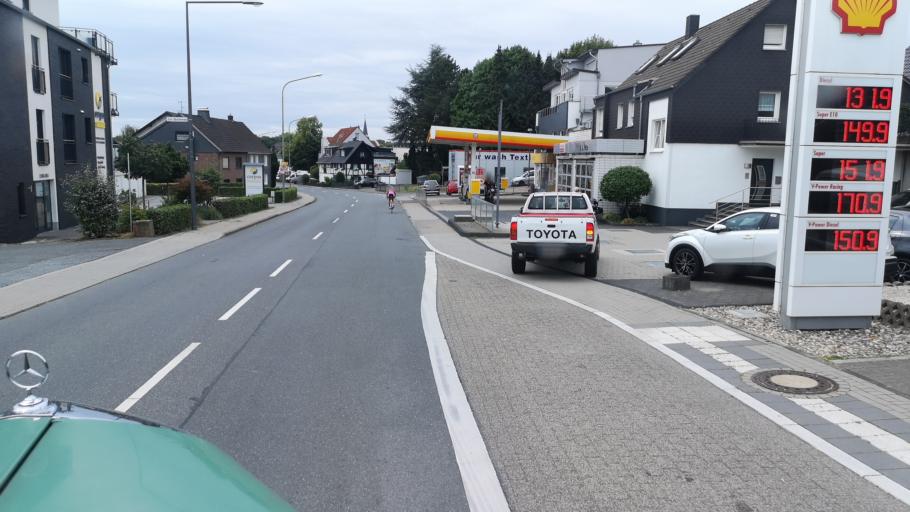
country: DE
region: North Rhine-Westphalia
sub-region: Regierungsbezirk Koln
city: Kurten
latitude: 51.0445
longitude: 7.2148
